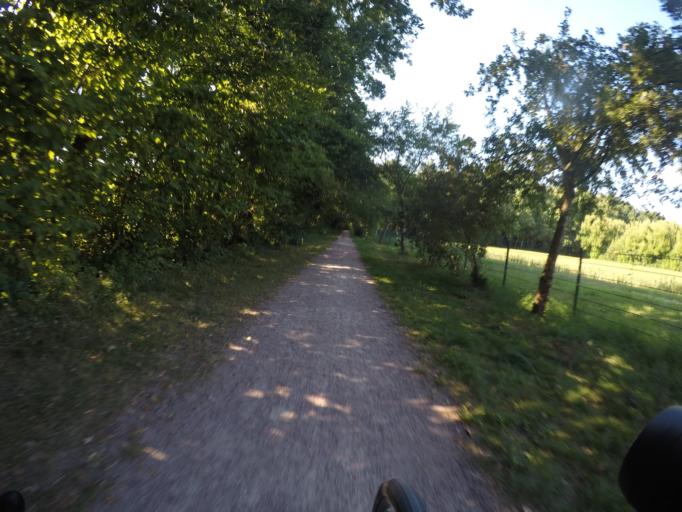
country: DE
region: Schleswig-Holstein
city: Oststeinbek
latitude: 53.5391
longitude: 10.1527
